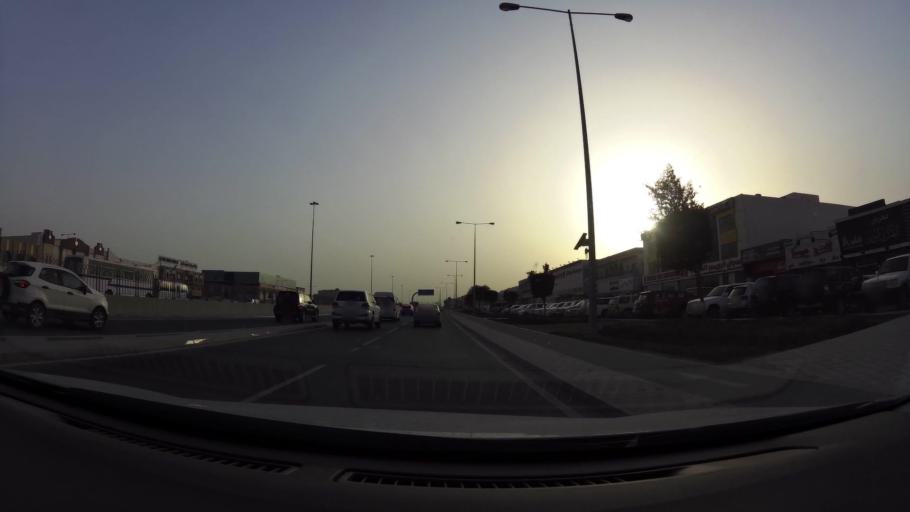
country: QA
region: Baladiyat ar Rayyan
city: Ar Rayyan
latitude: 25.2365
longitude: 51.4500
